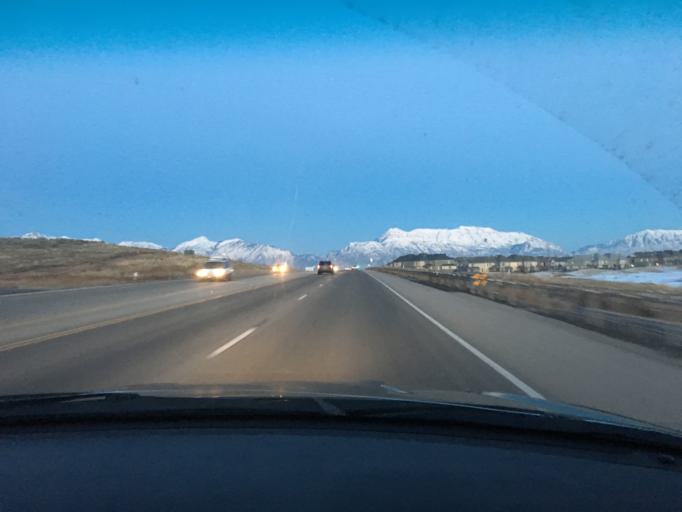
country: US
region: Utah
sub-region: Utah County
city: Saratoga Springs
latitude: 40.3813
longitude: -111.9703
